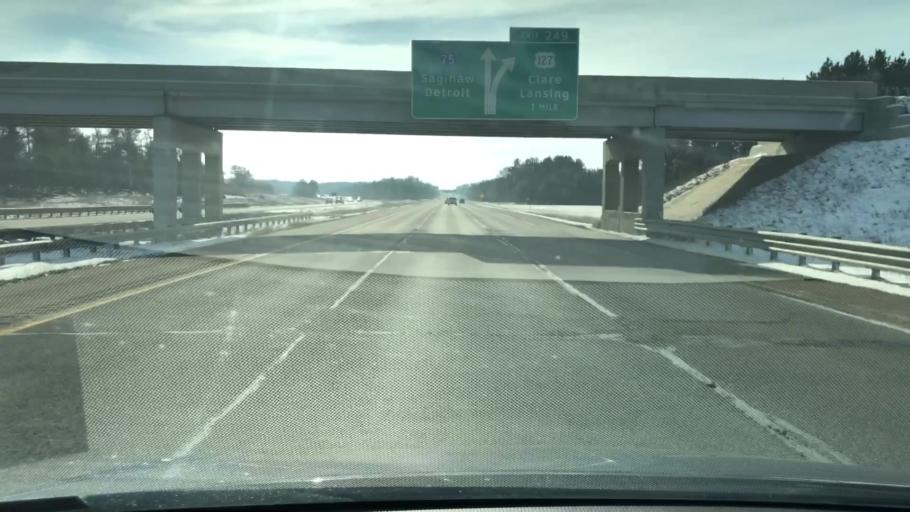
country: US
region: Michigan
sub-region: Crawford County
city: Grayling
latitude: 44.5987
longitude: -84.7093
